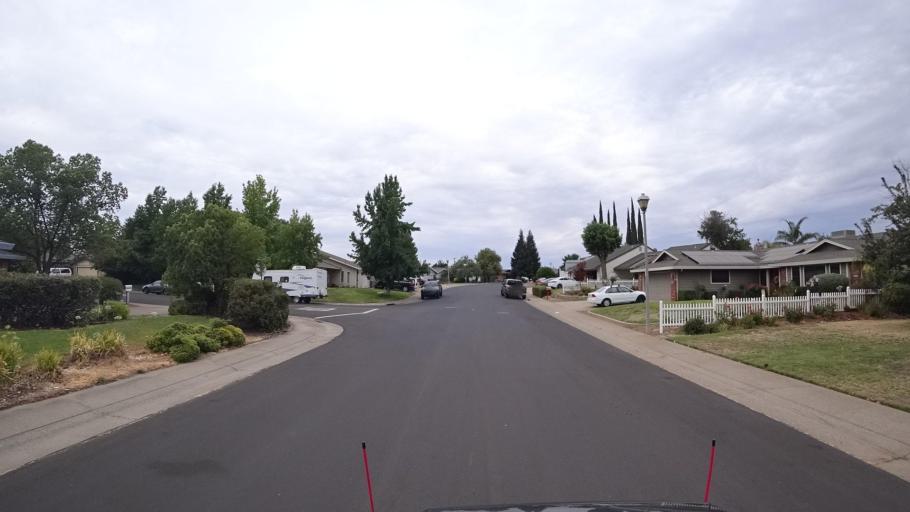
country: US
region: California
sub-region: Placer County
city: Rocklin
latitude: 38.7745
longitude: -121.2446
